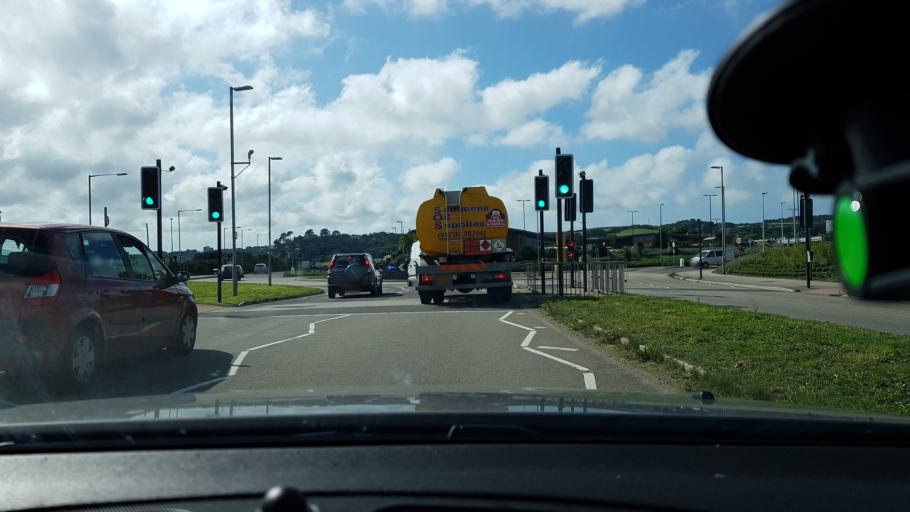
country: GB
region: England
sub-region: Cornwall
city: Penzance
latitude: 50.1277
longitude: -5.5154
